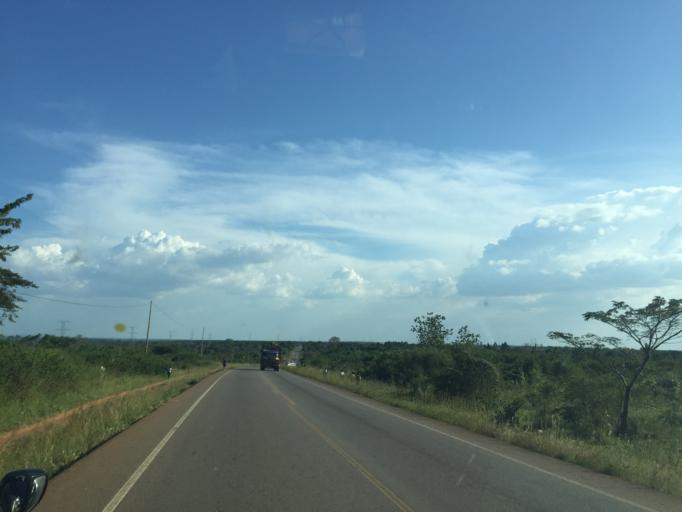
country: UG
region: Central Region
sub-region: Nakasongola District
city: Nakasongola
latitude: 1.2451
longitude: 32.4619
